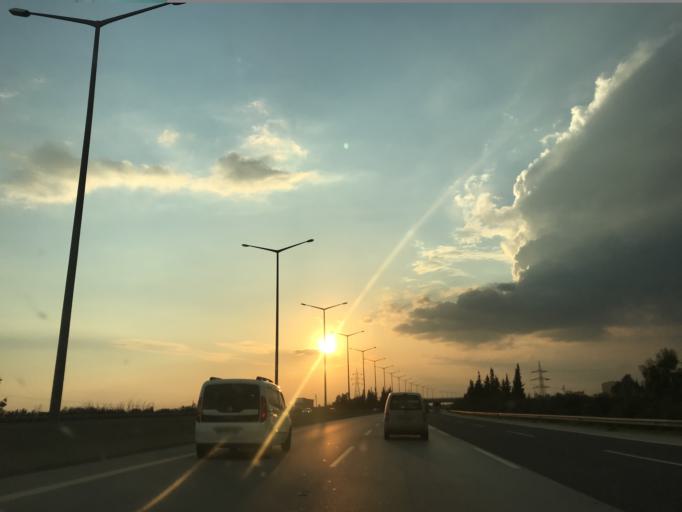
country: TR
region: Adana
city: Seyhan
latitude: 37.0297
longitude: 35.2292
